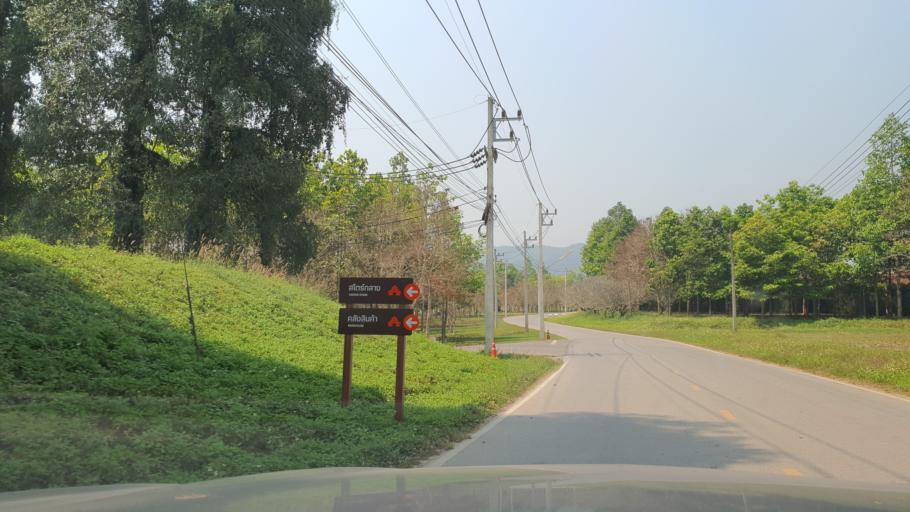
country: TH
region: Chiang Rai
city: Mae Lao
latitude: 19.8582
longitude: 99.7359
